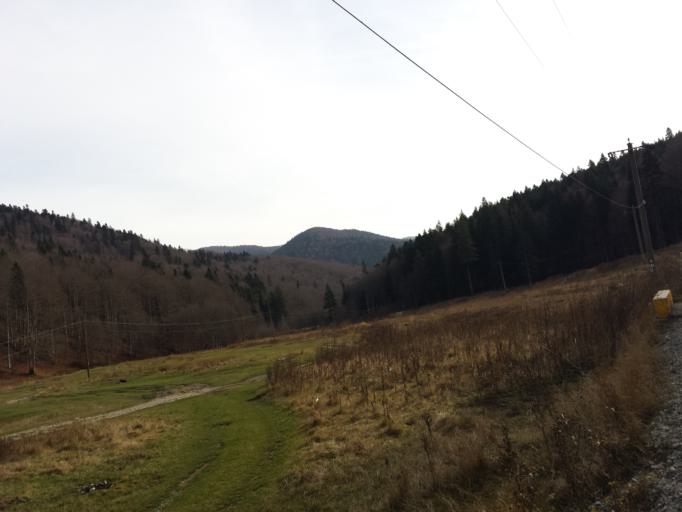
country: RO
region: Prahova
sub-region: Oras Azuga
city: Azuga
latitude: 45.4318
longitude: 25.5311
